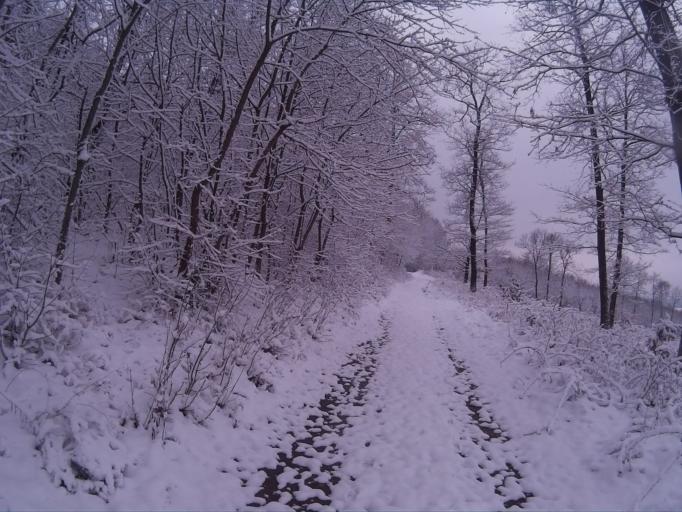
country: HU
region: Fejer
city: Szarliget
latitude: 47.5524
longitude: 18.5333
